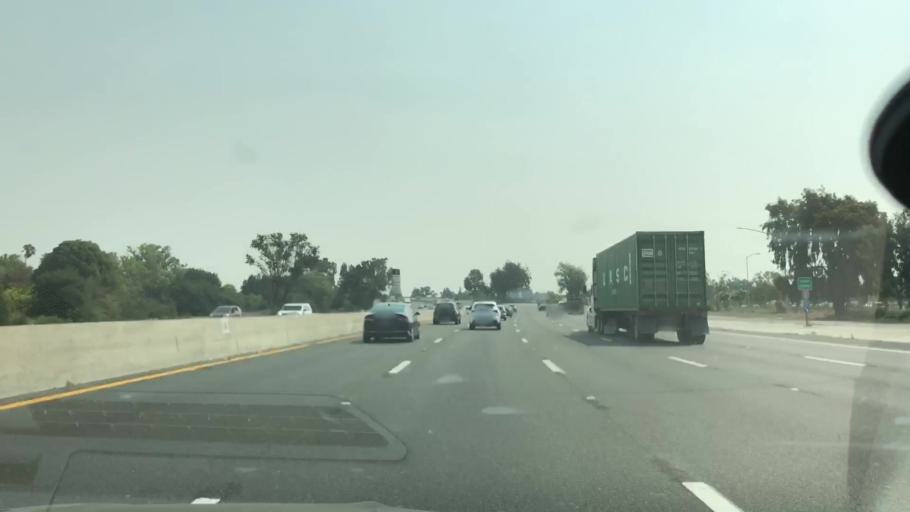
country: US
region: California
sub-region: Solano County
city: Fairfield
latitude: 38.2476
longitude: -122.0769
